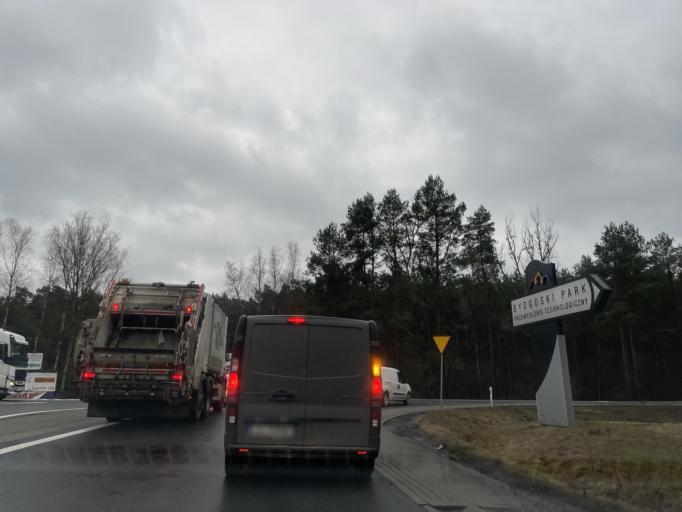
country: PL
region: Kujawsko-Pomorskie
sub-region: Powiat bydgoski
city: Nowa Wies Wielka
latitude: 53.0603
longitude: 18.0820
